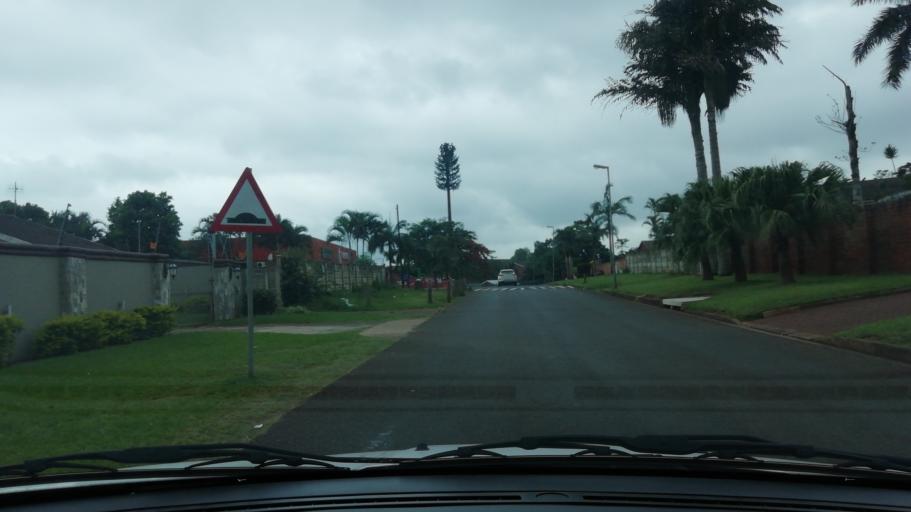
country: ZA
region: KwaZulu-Natal
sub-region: uThungulu District Municipality
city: Empangeni
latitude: -28.7660
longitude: 31.8982
